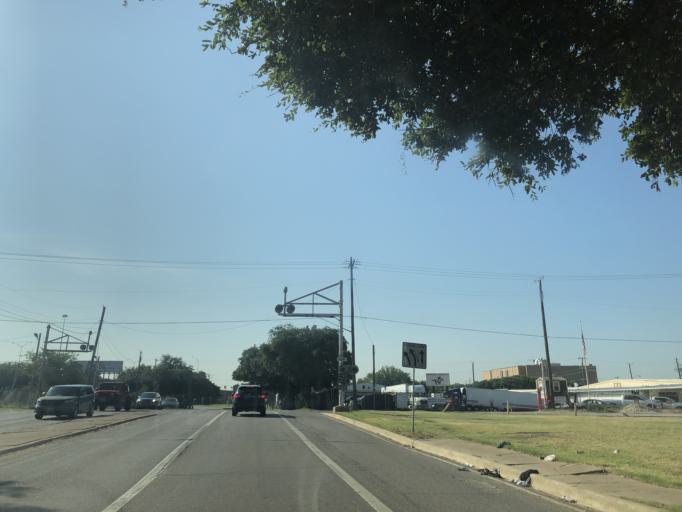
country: US
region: Texas
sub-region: Dallas County
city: Dallas
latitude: 32.7690
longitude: -96.7795
